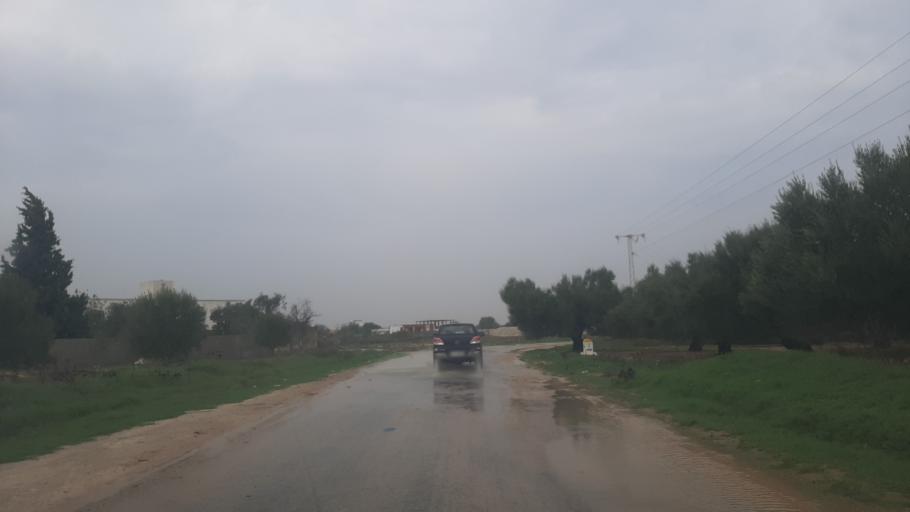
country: TN
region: Al Munastir
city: Sidi Bin Nur
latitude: 35.4744
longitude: 10.8781
